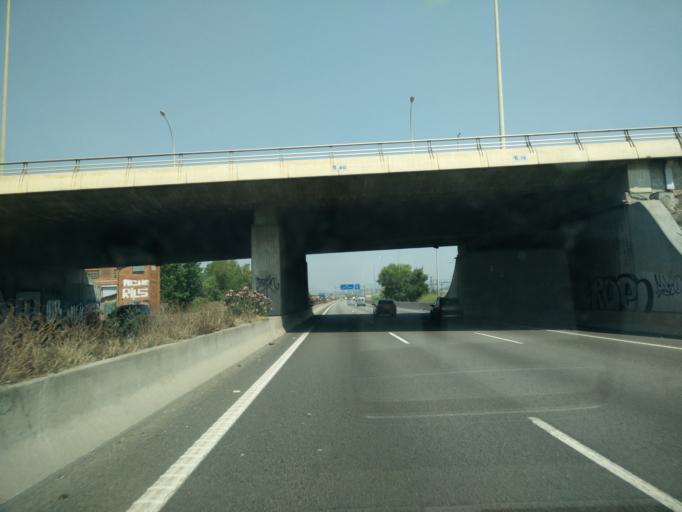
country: ES
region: Catalonia
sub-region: Provincia de Barcelona
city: Molins de Rei
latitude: 41.4073
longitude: 2.0102
